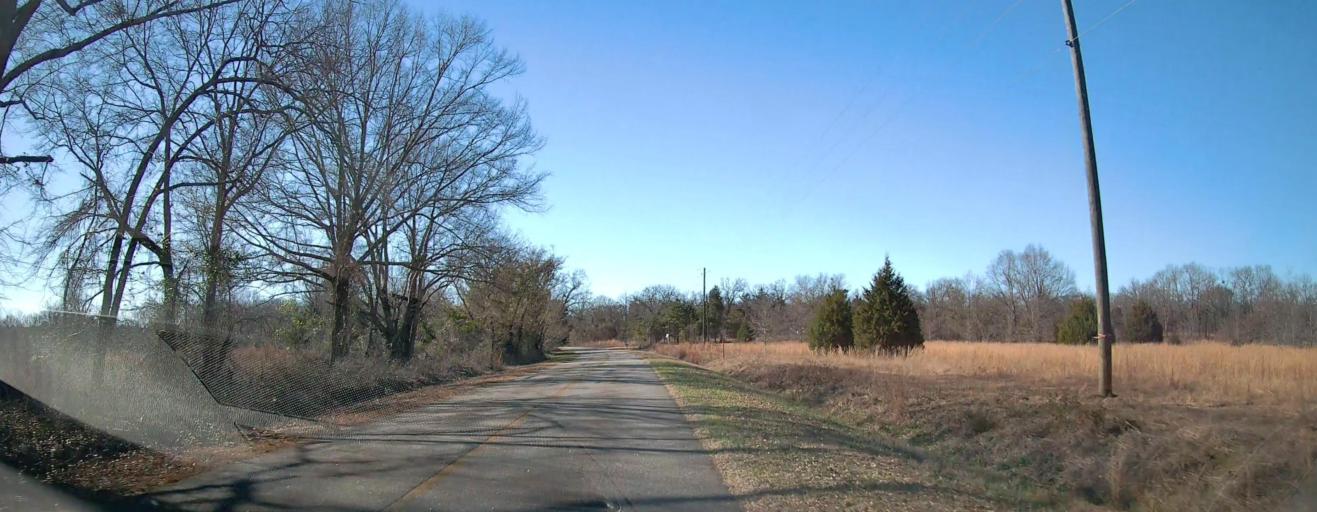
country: US
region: Georgia
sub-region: Taylor County
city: Butler
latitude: 32.6273
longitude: -84.2636
